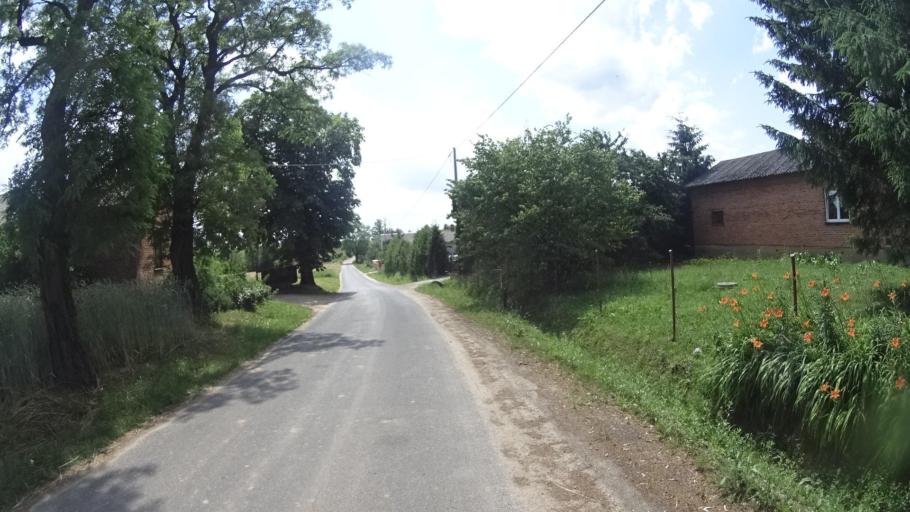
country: PL
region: Masovian Voivodeship
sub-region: Powiat grojecki
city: Goszczyn
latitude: 51.7135
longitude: 20.8322
